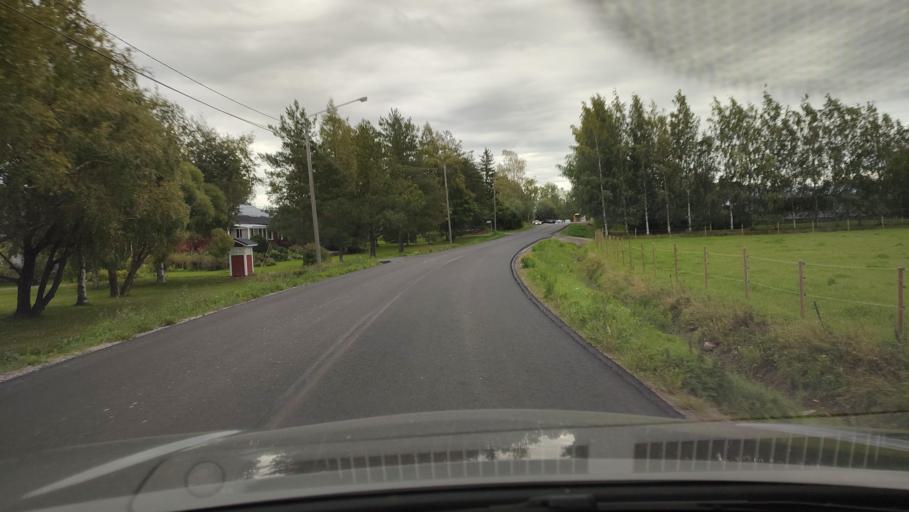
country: FI
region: Ostrobothnia
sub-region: Sydosterbotten
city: Kristinestad
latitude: 62.2489
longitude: 21.5340
